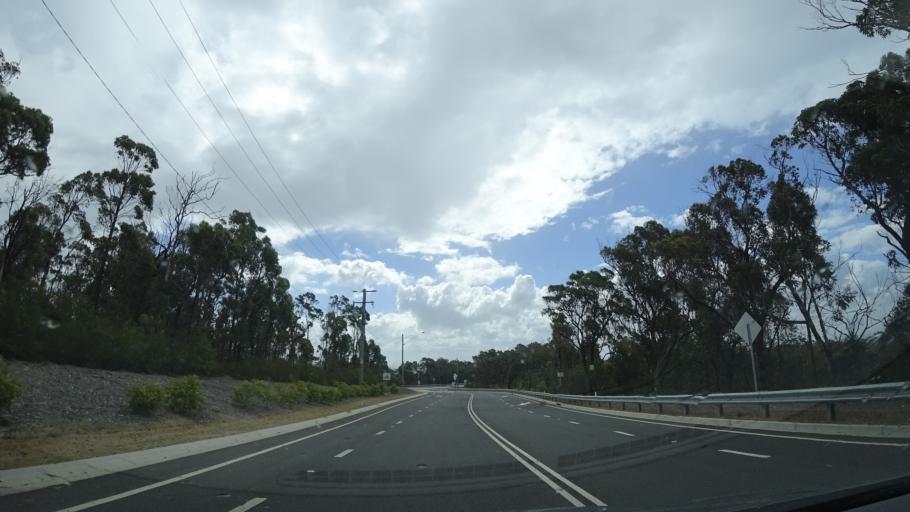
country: AU
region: New South Wales
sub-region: Wyong Shire
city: Kingfisher Shores
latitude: -33.1598
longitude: 151.6129
